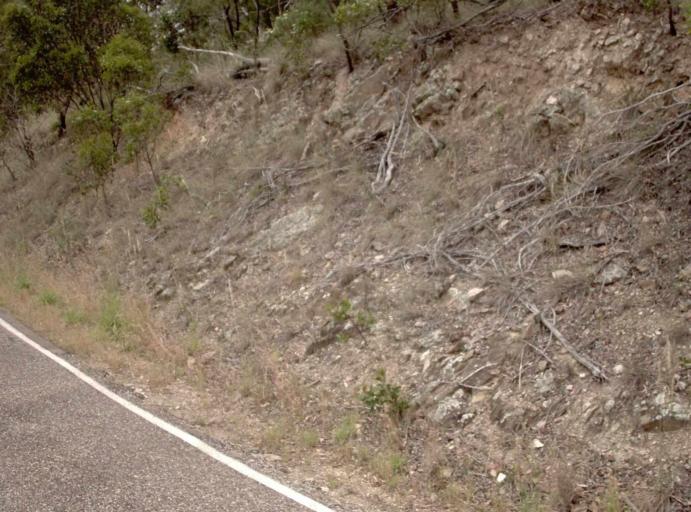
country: AU
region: Victoria
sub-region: East Gippsland
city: Bairnsdale
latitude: -37.5317
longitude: 147.2192
